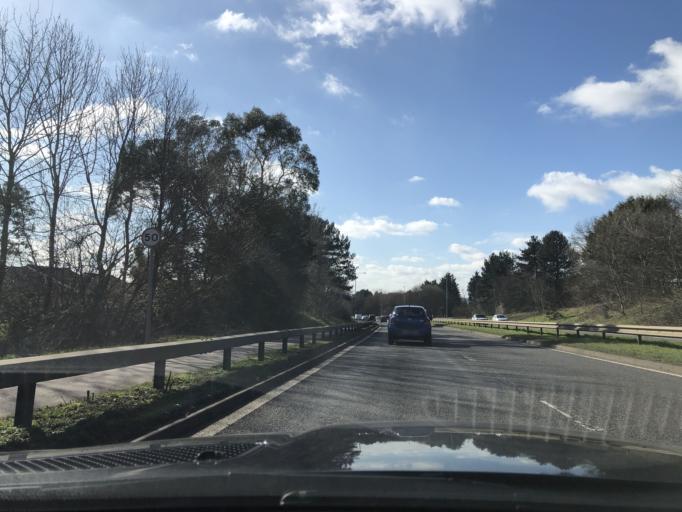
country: GB
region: England
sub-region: Northamptonshire
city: Northampton
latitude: 52.2496
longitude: -0.8364
